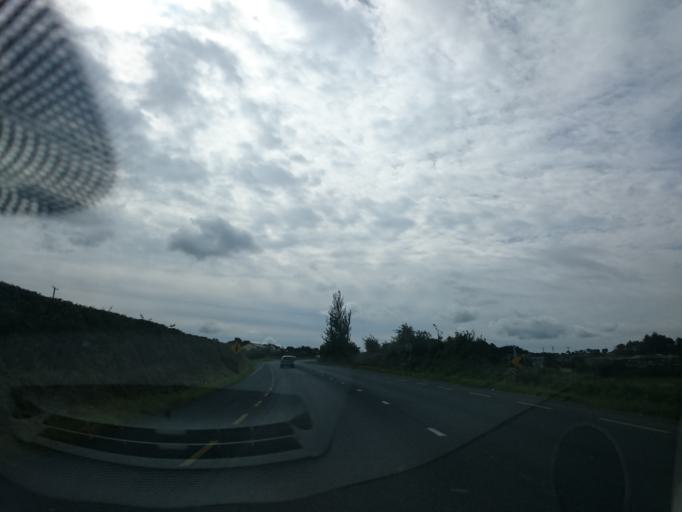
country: IE
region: Munster
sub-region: Waterford
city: Tra Mhor
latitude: 52.2244
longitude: -7.2001
